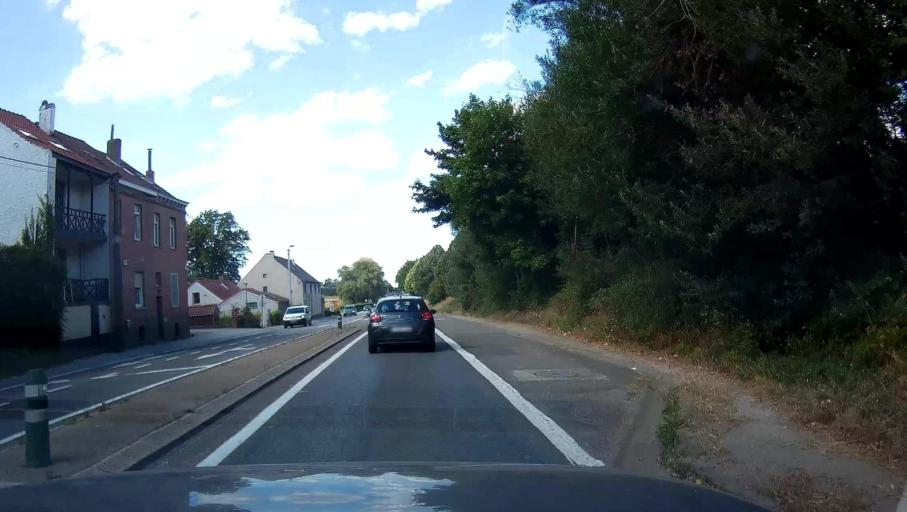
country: BE
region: Wallonia
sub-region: Province du Brabant Wallon
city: Waterloo
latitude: 50.6808
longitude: 4.4118
